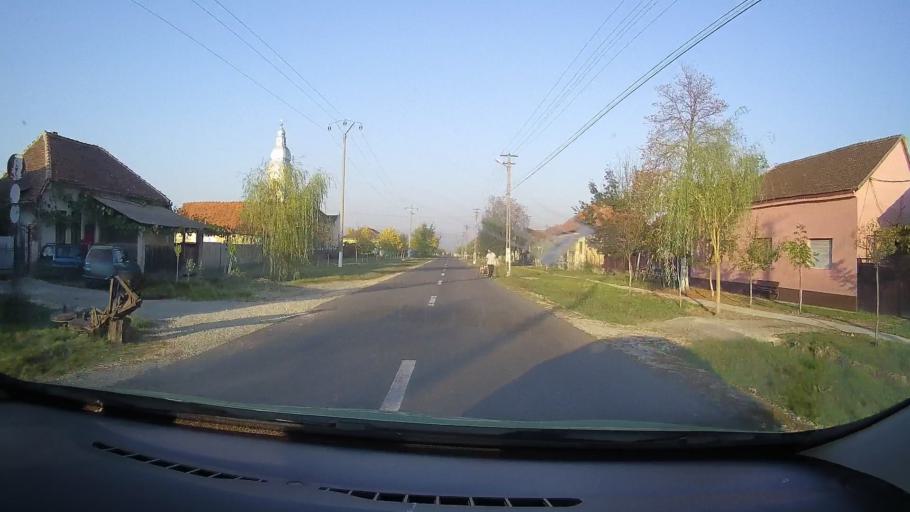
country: RO
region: Arad
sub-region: Comuna Barsa
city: Barsa
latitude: 46.3572
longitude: 22.0254
